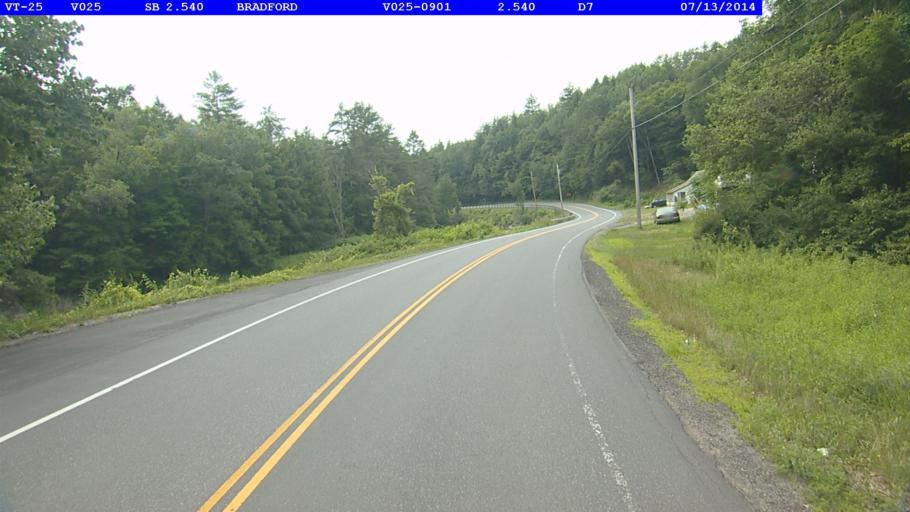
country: US
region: New Hampshire
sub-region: Grafton County
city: Orford
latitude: 43.9937
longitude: -72.1541
